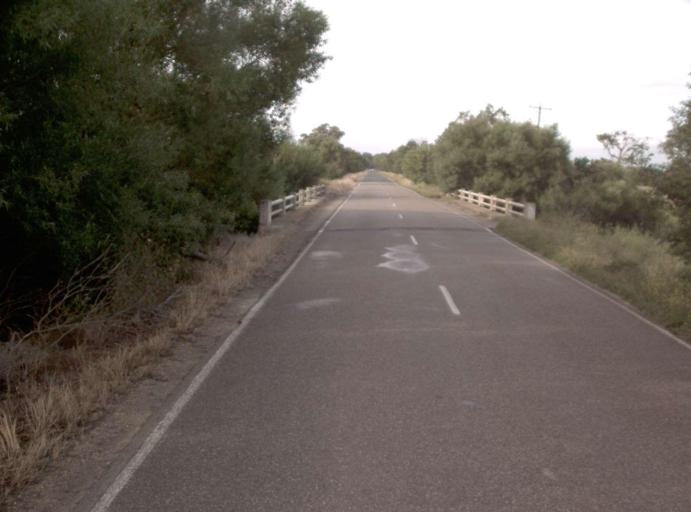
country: AU
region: Victoria
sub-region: Wellington
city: Heyfield
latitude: -37.9748
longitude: 146.8894
